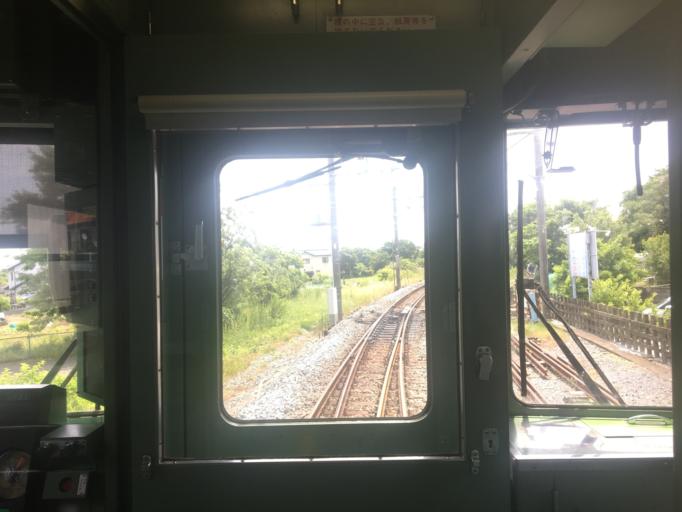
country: JP
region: Saitama
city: Morohongo
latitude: 35.9372
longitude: 139.3478
